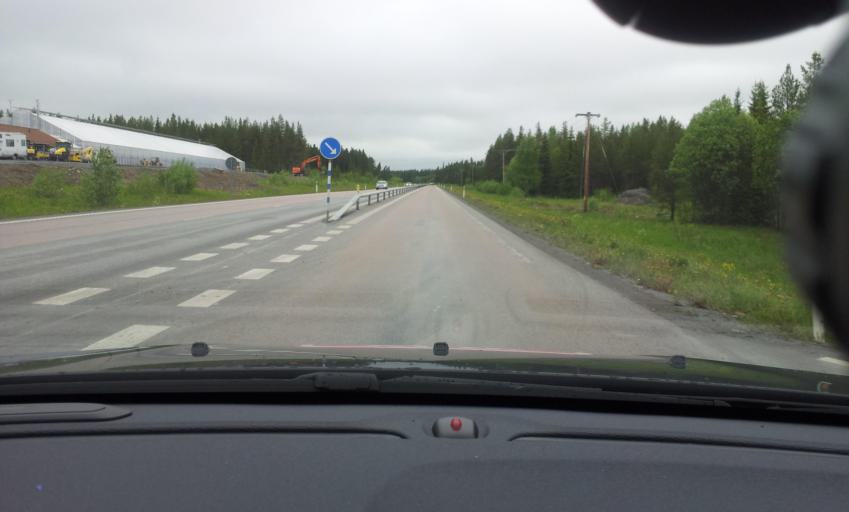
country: SE
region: Jaemtland
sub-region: OEstersunds Kommun
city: Ostersund
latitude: 63.2377
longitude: 14.6050
